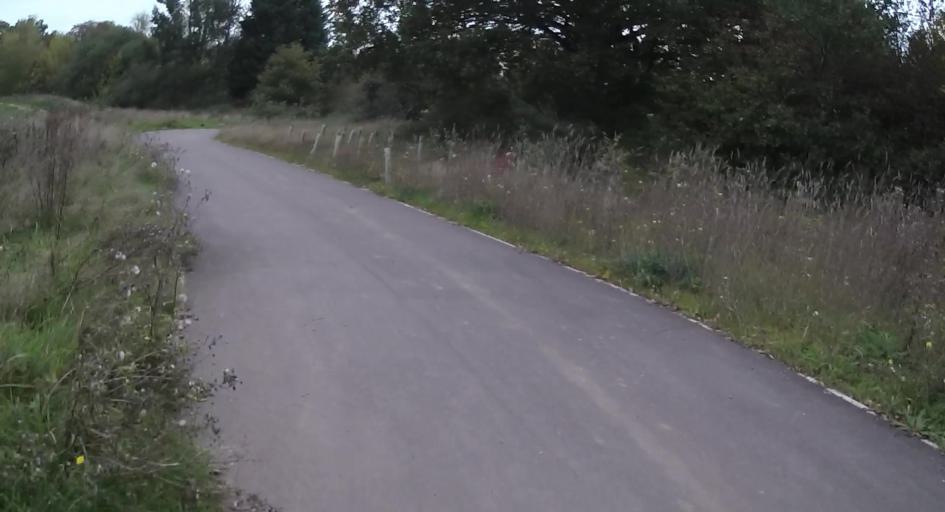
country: GB
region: England
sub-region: Bracknell Forest
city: Binfield
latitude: 51.4277
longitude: -0.7731
